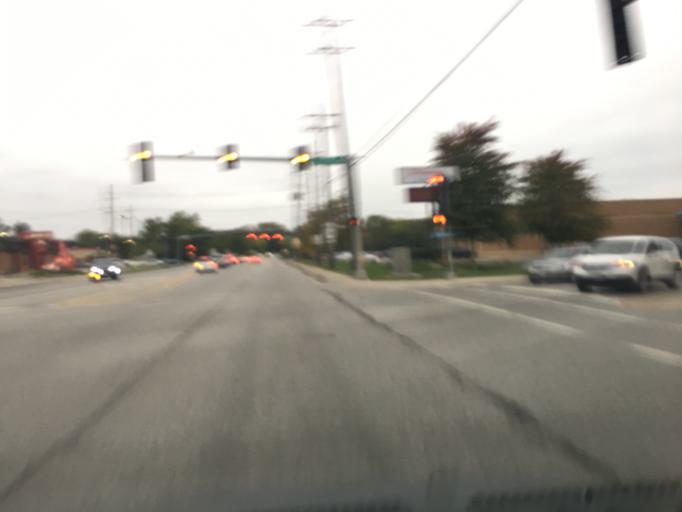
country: US
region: Illinois
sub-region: Cook County
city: Lyons
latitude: 41.8146
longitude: -87.8338
